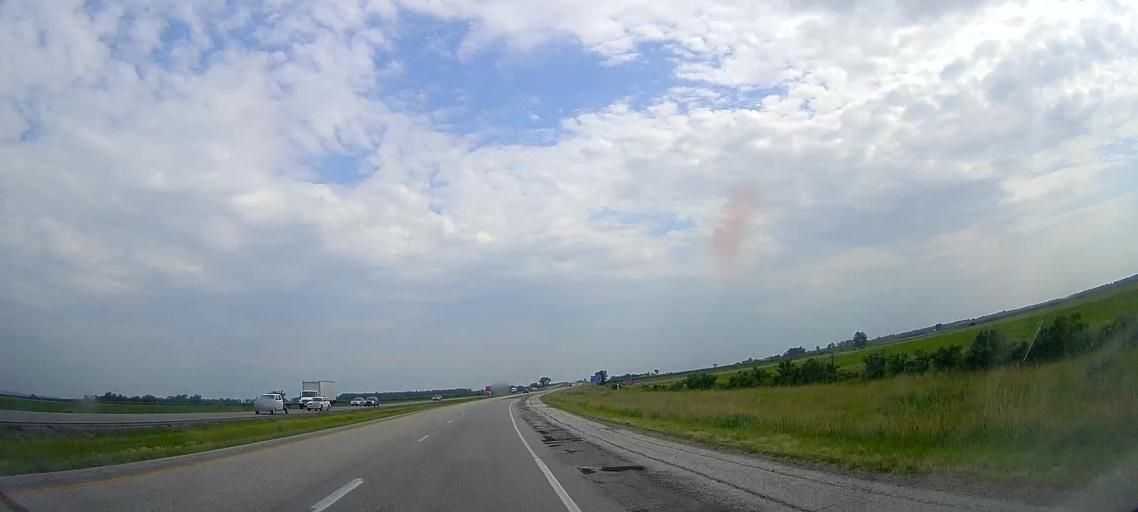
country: US
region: Nebraska
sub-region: Burt County
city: Tekamah
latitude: 41.7591
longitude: -96.0456
